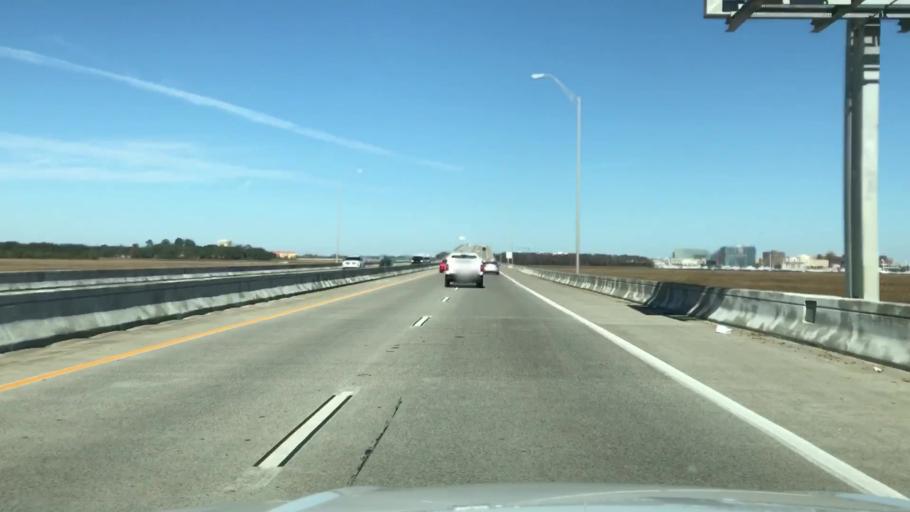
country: US
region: South Carolina
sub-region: Charleston County
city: Charleston
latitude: 32.7617
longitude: -79.9579
